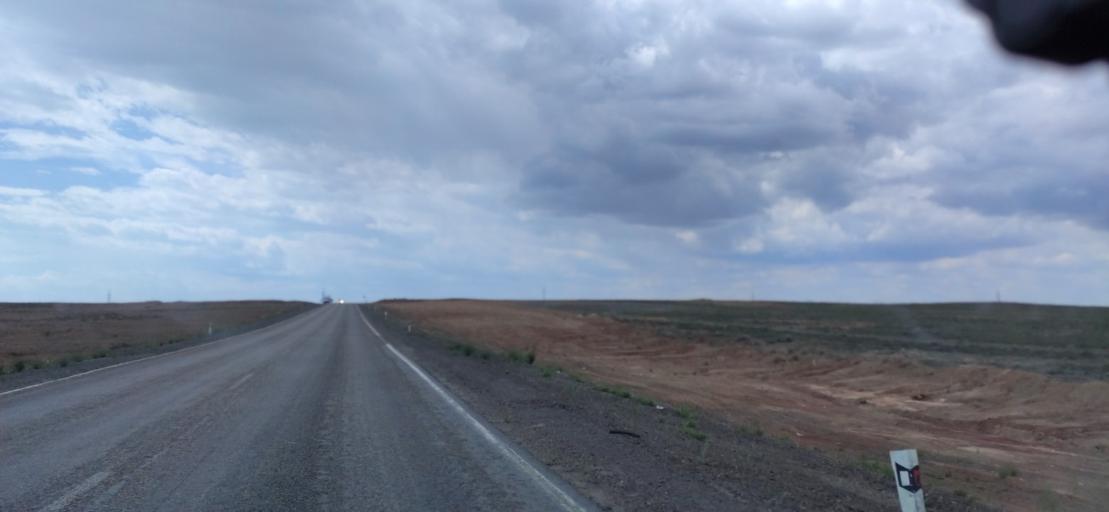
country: KZ
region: Qaraghandy
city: Saryshaghan
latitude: 46.0709
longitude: 73.6019
